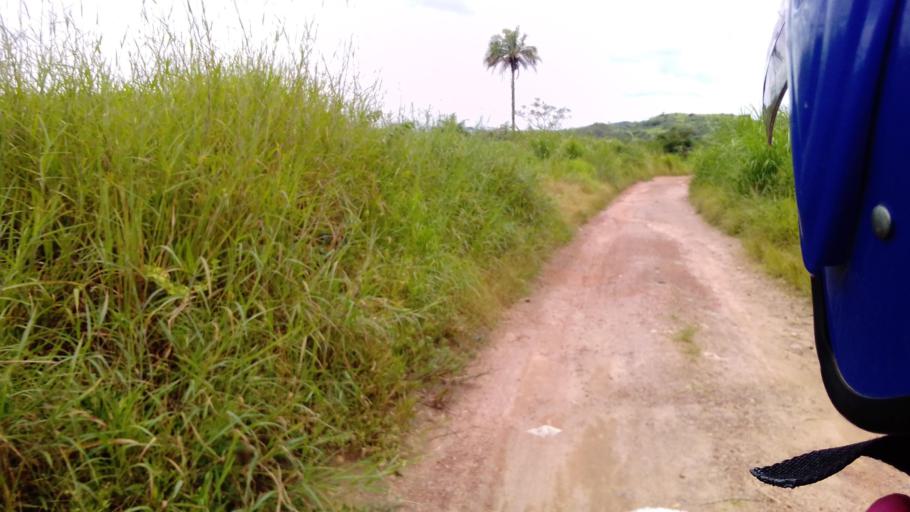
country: SL
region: Eastern Province
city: Koidu
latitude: 8.6671
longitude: -10.9489
